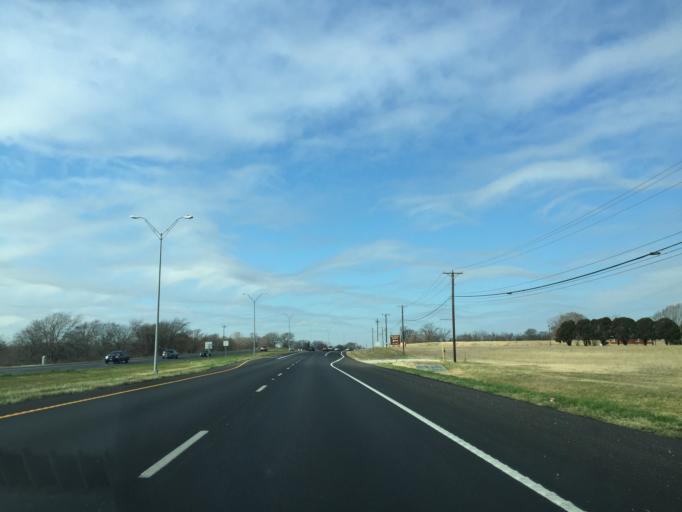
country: US
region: Texas
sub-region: Williamson County
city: Round Rock
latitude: 30.5209
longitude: -97.6429
